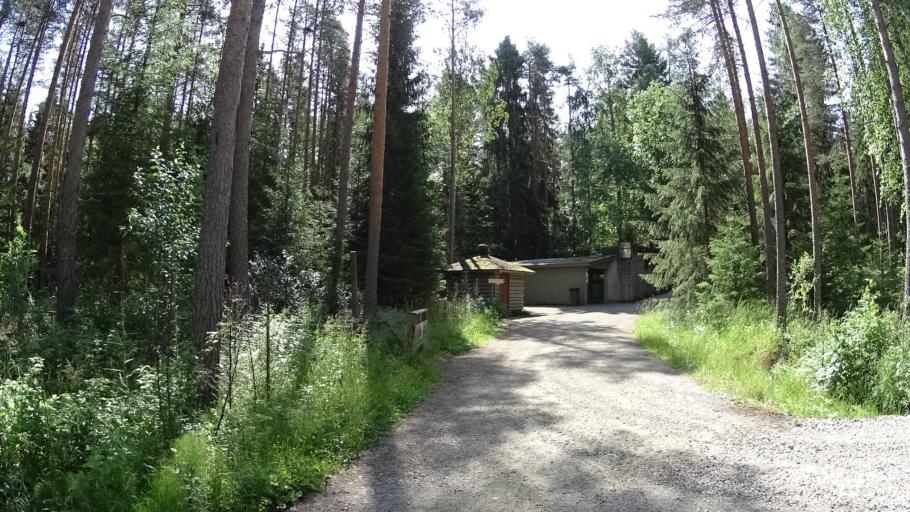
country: FI
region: Southern Ostrobothnia
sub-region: Kuusiokunnat
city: AEhtaeri
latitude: 62.5394
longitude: 24.1844
